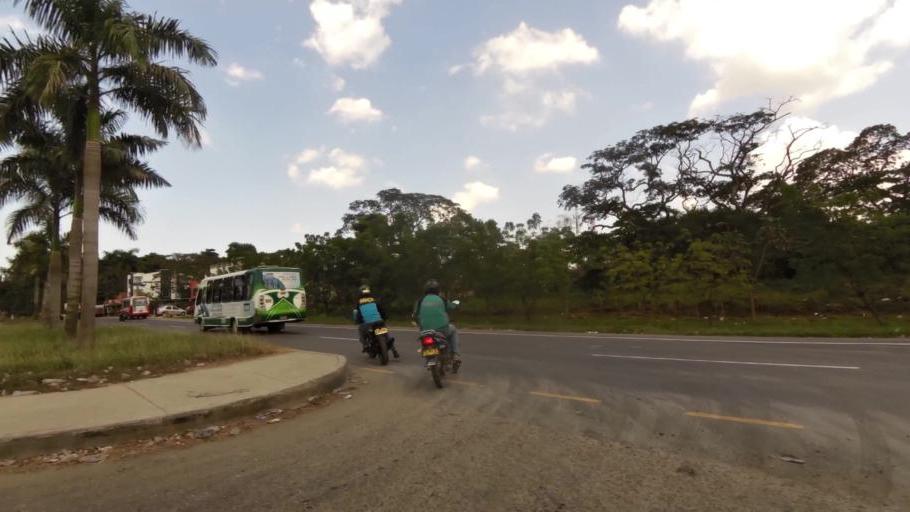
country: CO
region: Bolivar
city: Cartagena
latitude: 10.3734
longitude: -75.4572
